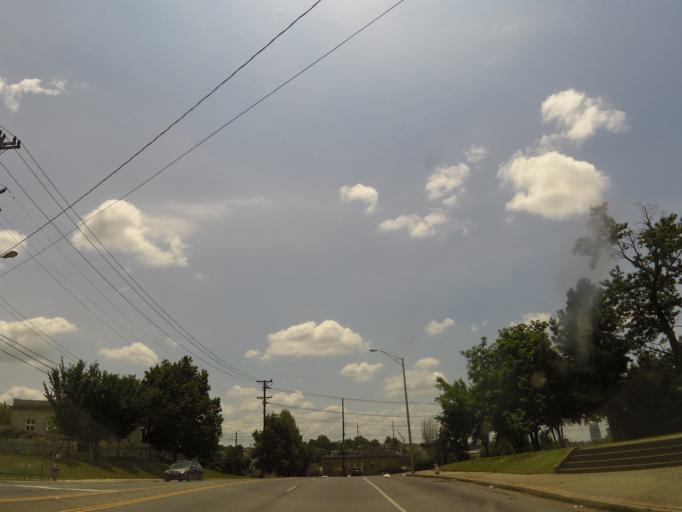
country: US
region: Tennessee
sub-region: Davidson County
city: Nashville
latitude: 36.1797
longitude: -86.7501
